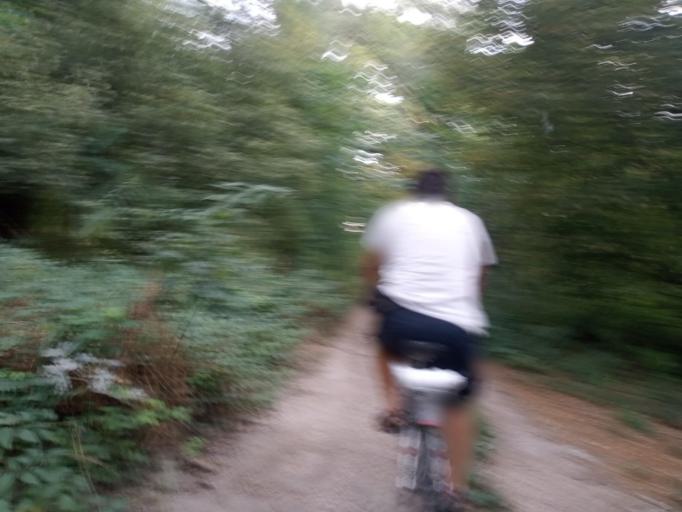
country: HU
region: Pest
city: Szentendre
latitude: 47.6390
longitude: 19.0820
